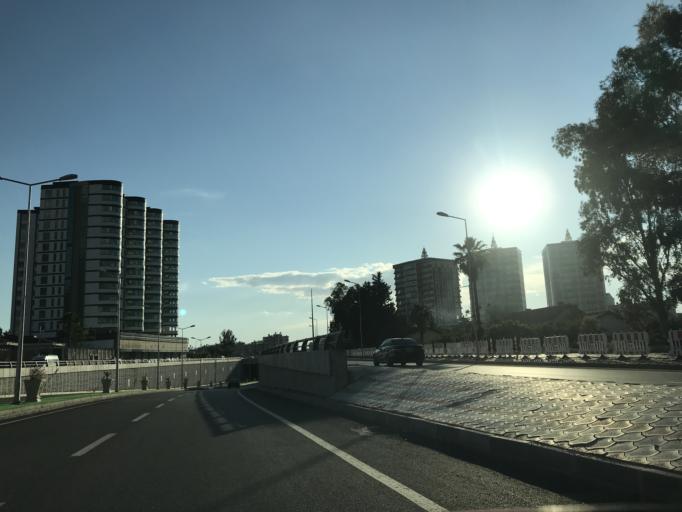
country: TR
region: Hatay
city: Iskenderun
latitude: 36.5854
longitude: 36.1784
